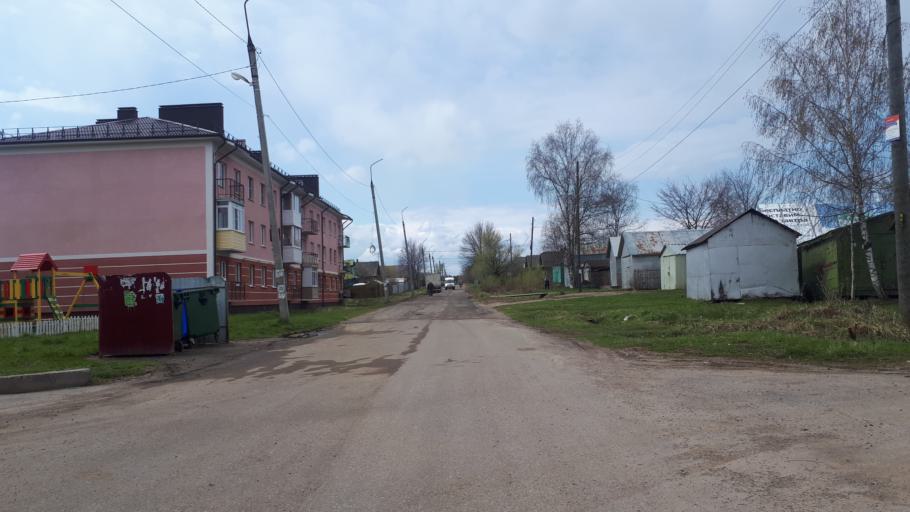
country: RU
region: Jaroslavl
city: Konstantinovskiy
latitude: 57.8283
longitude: 39.5837
